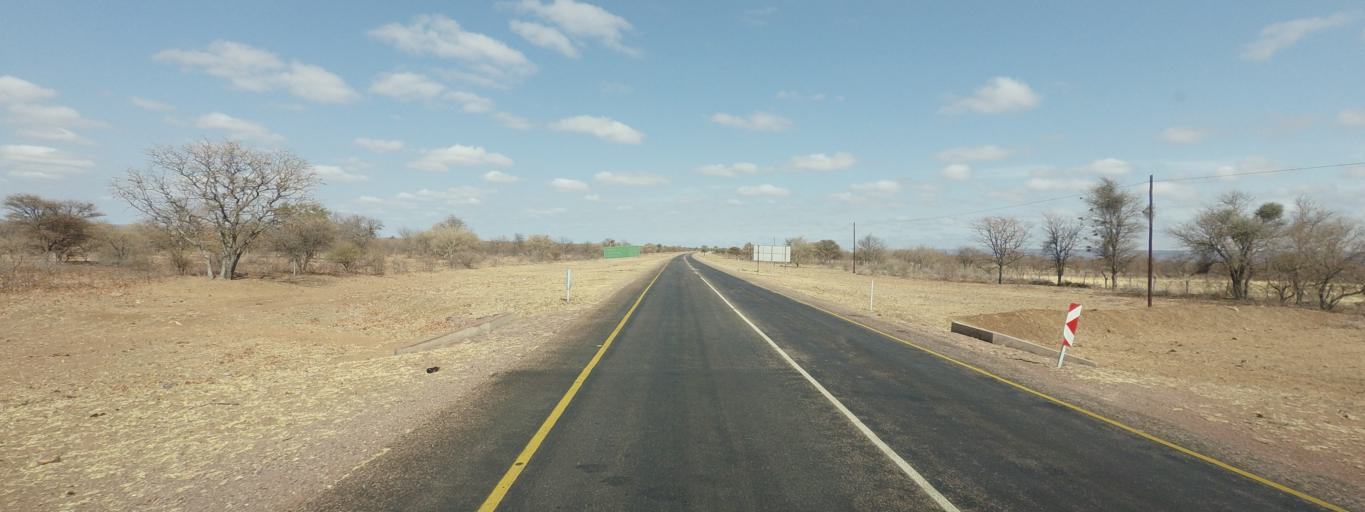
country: BW
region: Central
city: Ramokgonami
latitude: -22.8011
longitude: 27.4904
